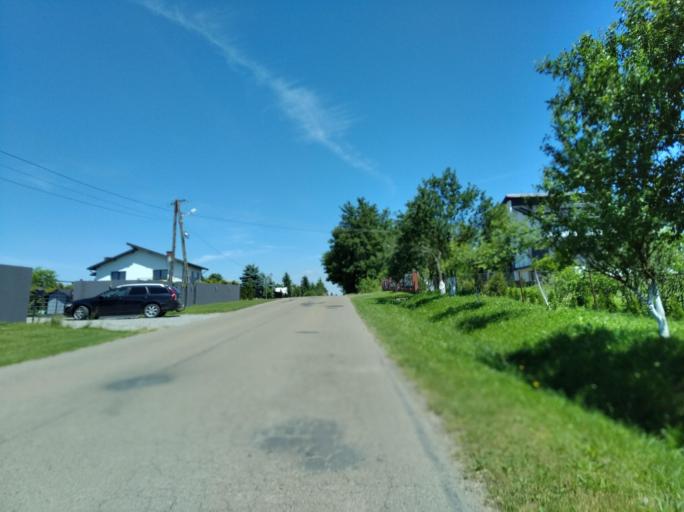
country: PL
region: Subcarpathian Voivodeship
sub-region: Powiat jasielski
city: Tarnowiec
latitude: 49.7216
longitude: 21.5618
